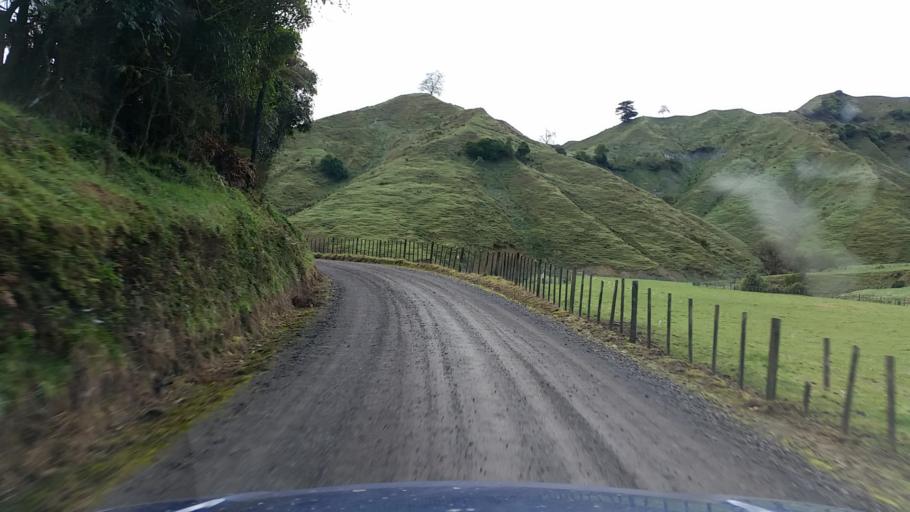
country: NZ
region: Taranaki
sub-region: New Plymouth District
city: Waitara
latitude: -39.0950
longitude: 174.8393
